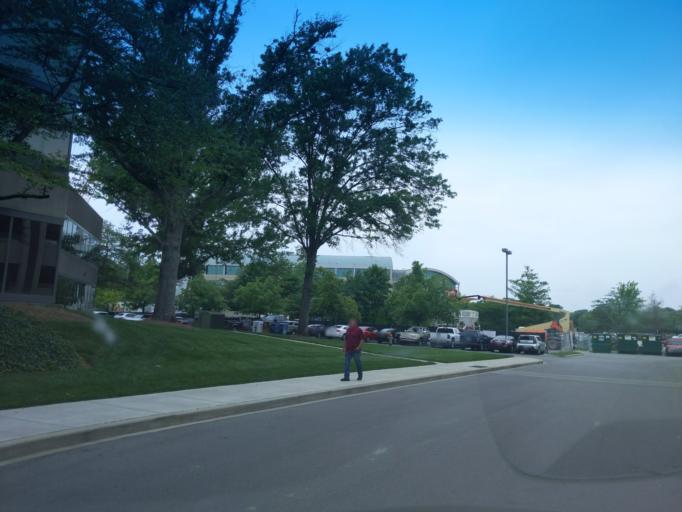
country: US
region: Tennessee
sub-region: Williamson County
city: Brentwood
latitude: 36.0423
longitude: -86.7742
